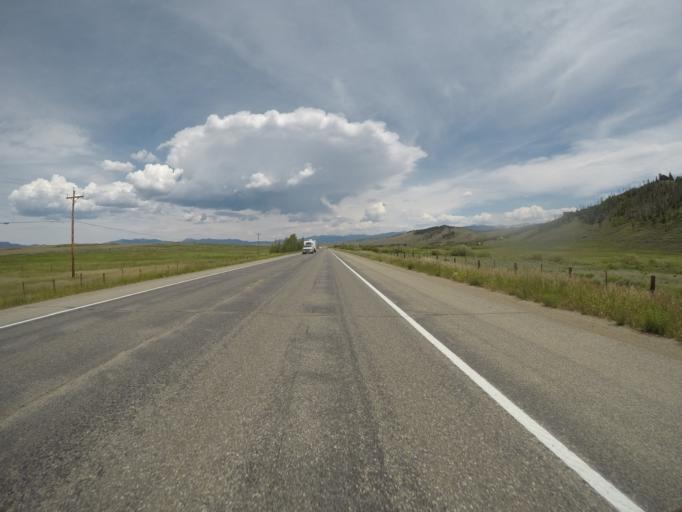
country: US
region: Colorado
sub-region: Grand County
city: Granby
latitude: 40.0499
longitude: -105.9331
